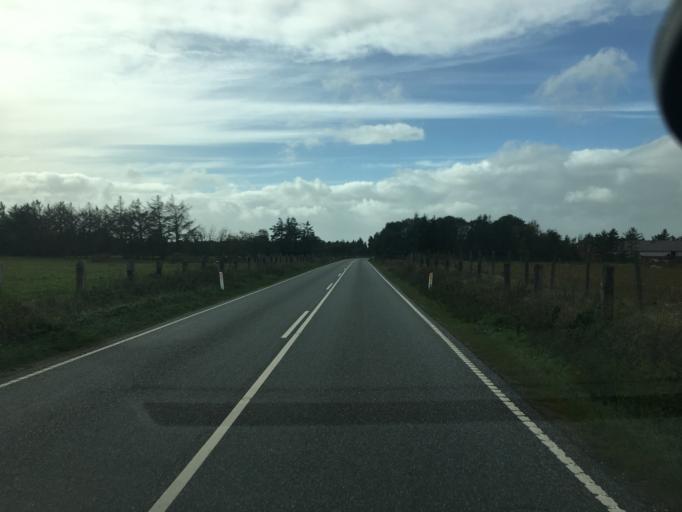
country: DK
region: South Denmark
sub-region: Tonder Kommune
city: Tonder
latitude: 55.0101
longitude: 8.8339
